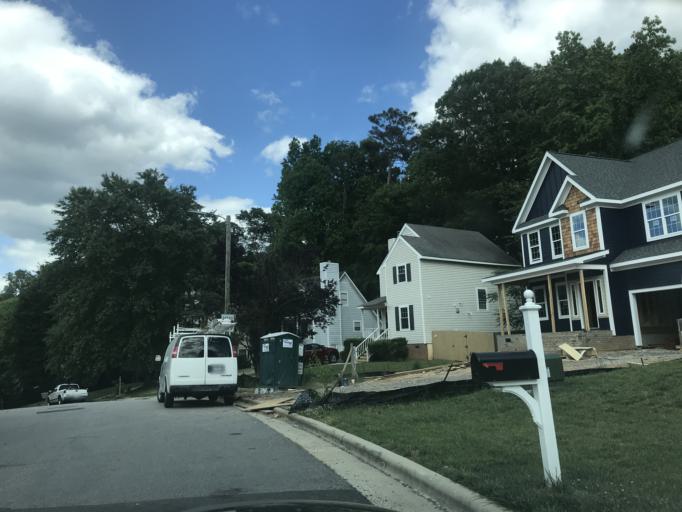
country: US
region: North Carolina
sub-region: Wake County
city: Raleigh
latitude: 35.8104
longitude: -78.6224
